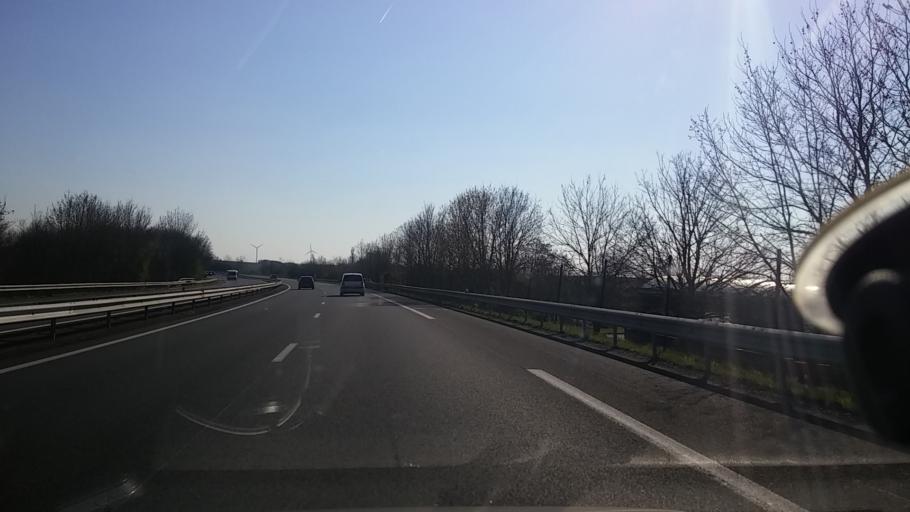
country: FR
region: Centre
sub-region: Departement de l'Indre
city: Vatan
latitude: 47.0484
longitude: 1.7997
